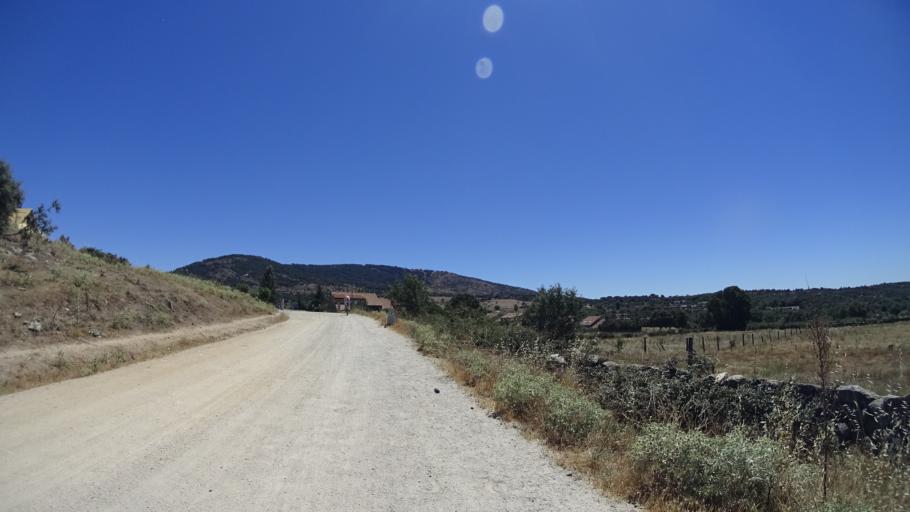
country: ES
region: Madrid
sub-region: Provincia de Madrid
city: Collado Mediano
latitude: 40.6884
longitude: -4.0306
